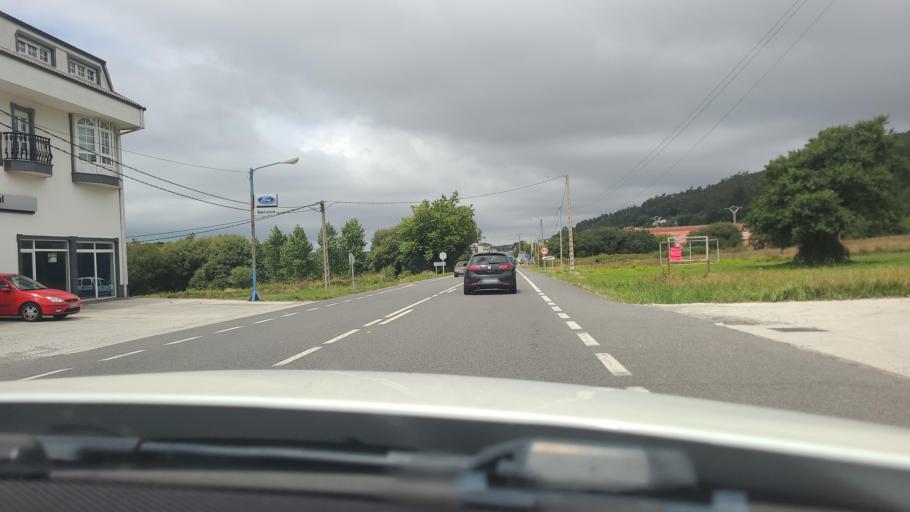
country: ES
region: Galicia
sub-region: Provincia da Coruna
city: Cee
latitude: 42.9832
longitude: -9.1863
